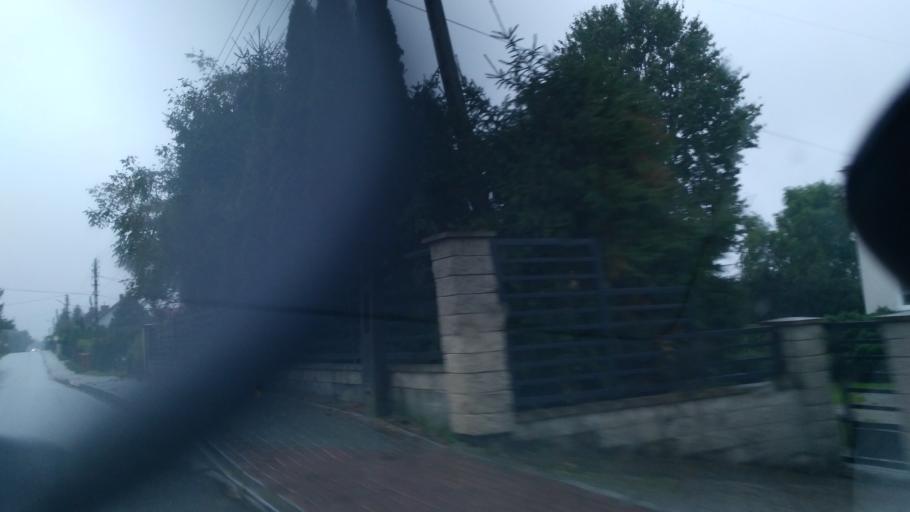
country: PL
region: Subcarpathian Voivodeship
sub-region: Powiat krosnienski
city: Miejsce Piastowe
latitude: 49.6534
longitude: 21.8072
